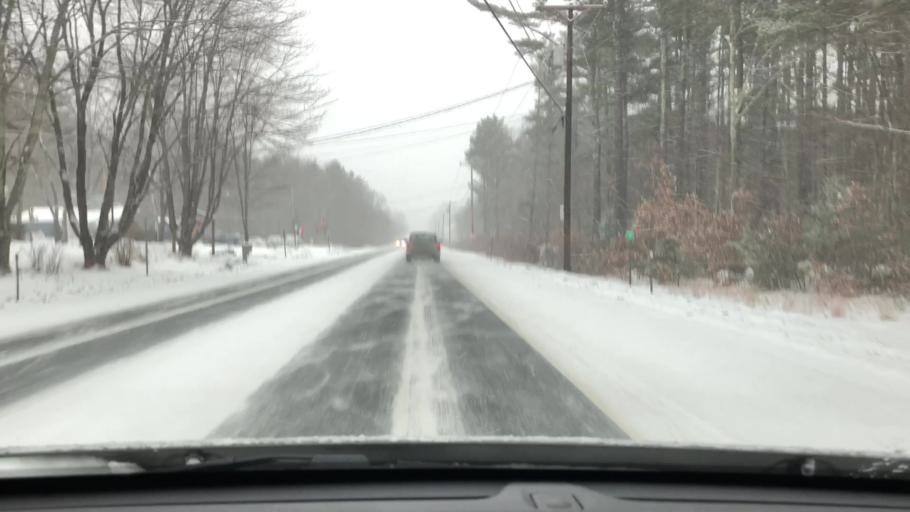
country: US
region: New Hampshire
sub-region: Strafford County
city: Barrington
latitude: 43.1844
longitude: -70.9991
